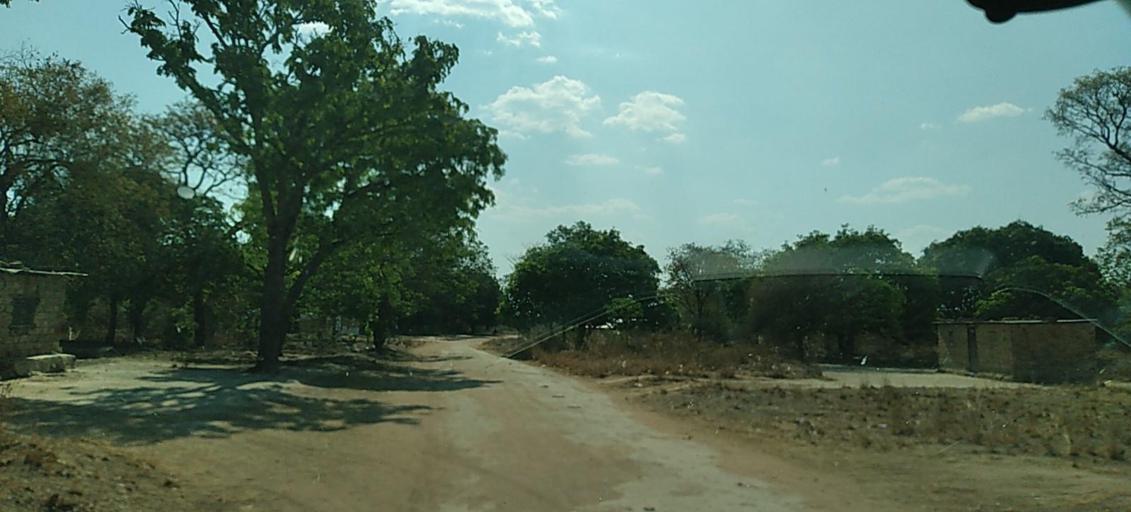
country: ZM
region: North-Western
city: Kalengwa
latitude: -13.1316
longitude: 25.0140
